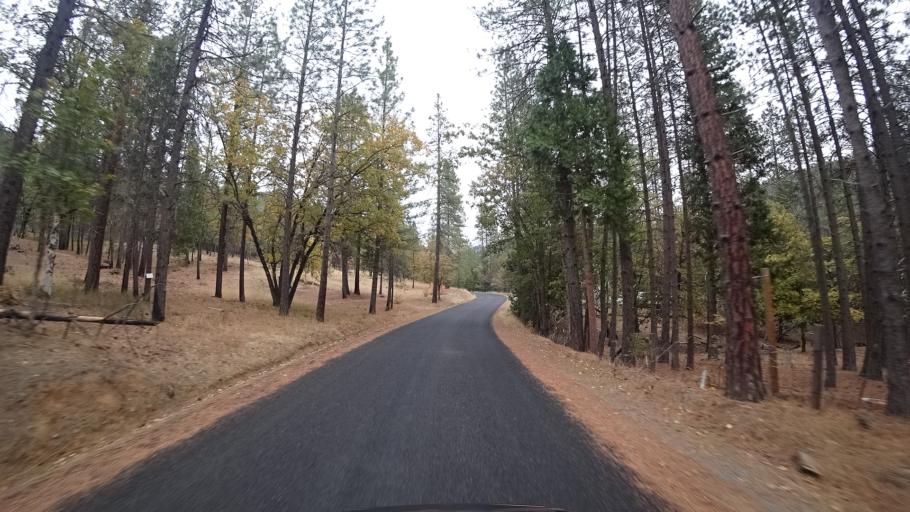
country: US
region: California
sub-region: Siskiyou County
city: Happy Camp
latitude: 41.8563
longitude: -123.1691
